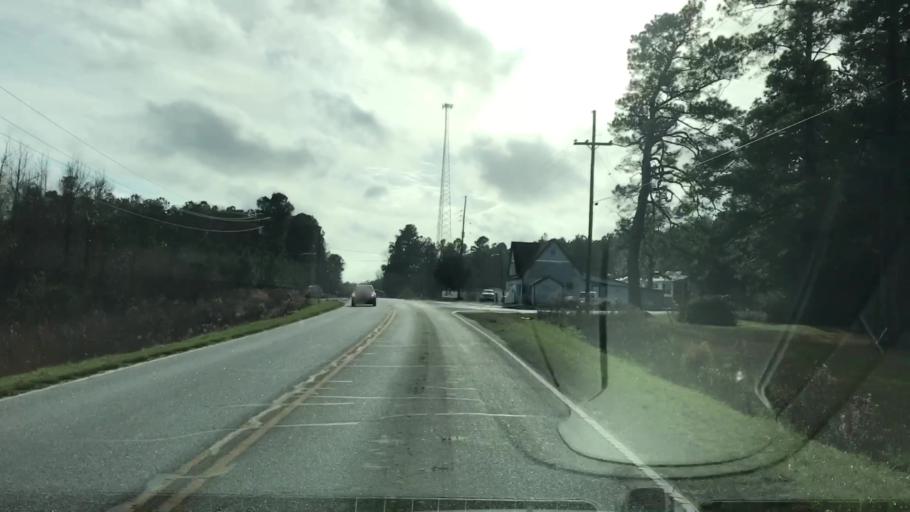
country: US
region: South Carolina
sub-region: Williamsburg County
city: Andrews
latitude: 33.3589
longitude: -79.6554
